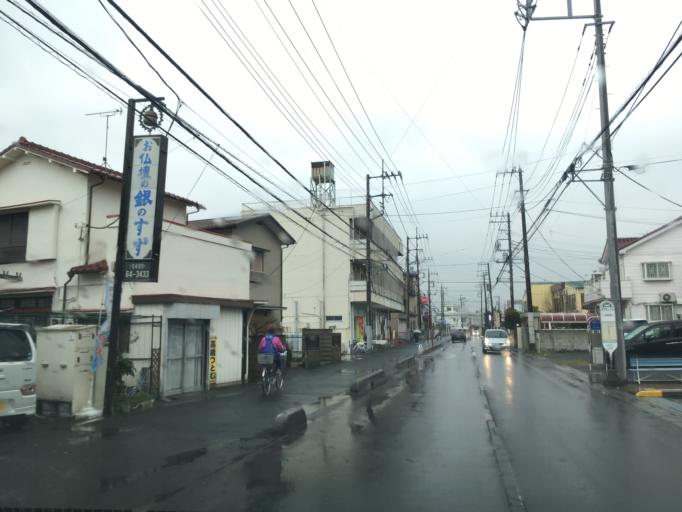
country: JP
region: Saitama
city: Koshigaya
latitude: 35.8909
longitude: 139.7790
